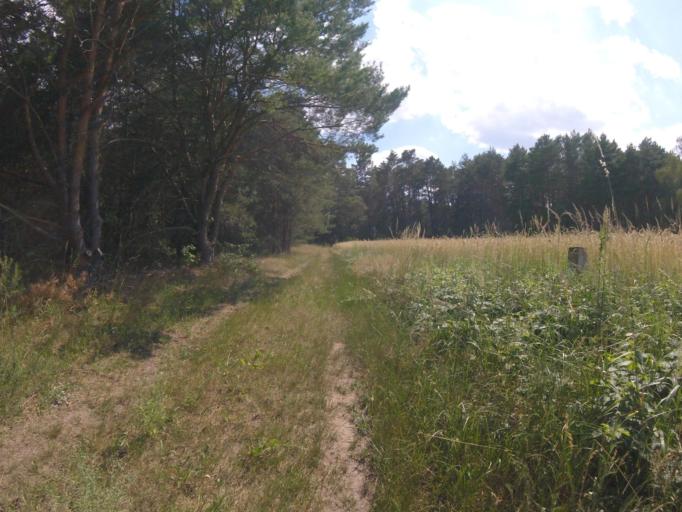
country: DE
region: Brandenburg
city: Wildau
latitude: 52.3317
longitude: 13.6761
